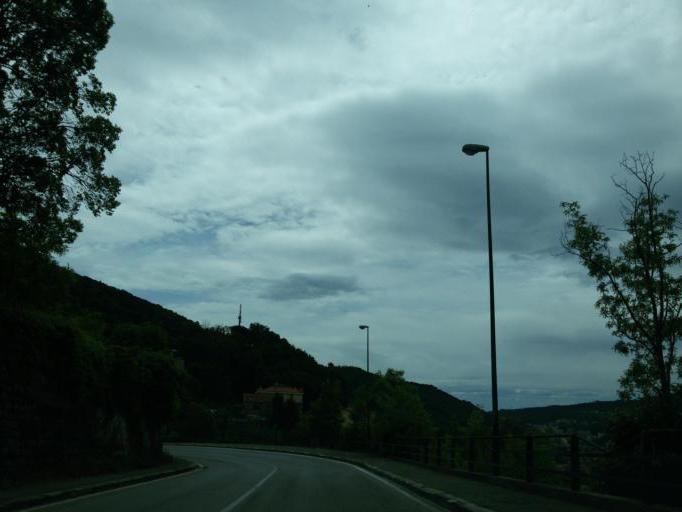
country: IT
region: Liguria
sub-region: Provincia di Genova
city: Piccarello
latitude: 44.4422
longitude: 8.9853
